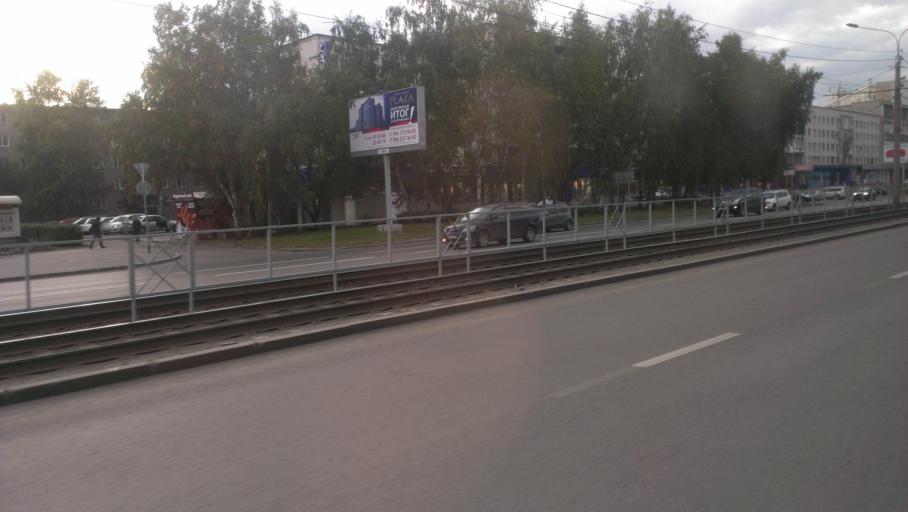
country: RU
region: Altai Krai
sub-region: Gorod Barnaulskiy
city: Barnaul
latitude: 53.3454
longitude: 83.7657
